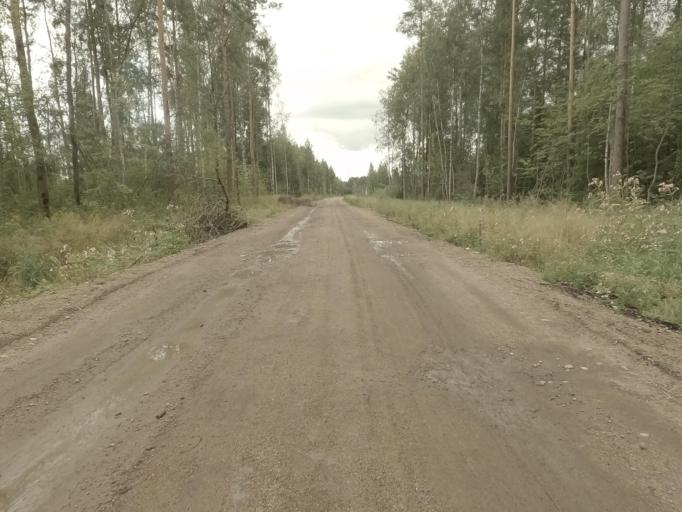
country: RU
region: Leningrad
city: Kirovsk
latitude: 59.9025
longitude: 31.0033
